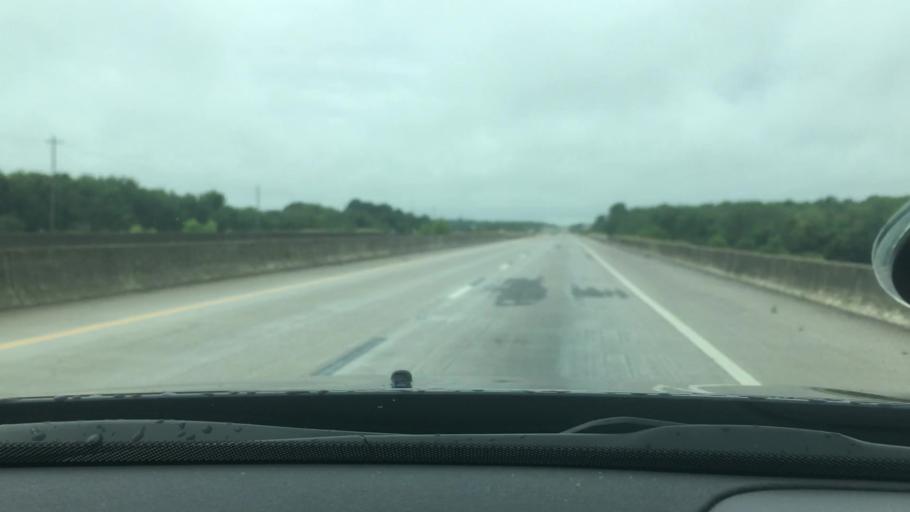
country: US
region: Oklahoma
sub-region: Atoka County
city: Atoka
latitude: 34.2602
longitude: -96.2114
